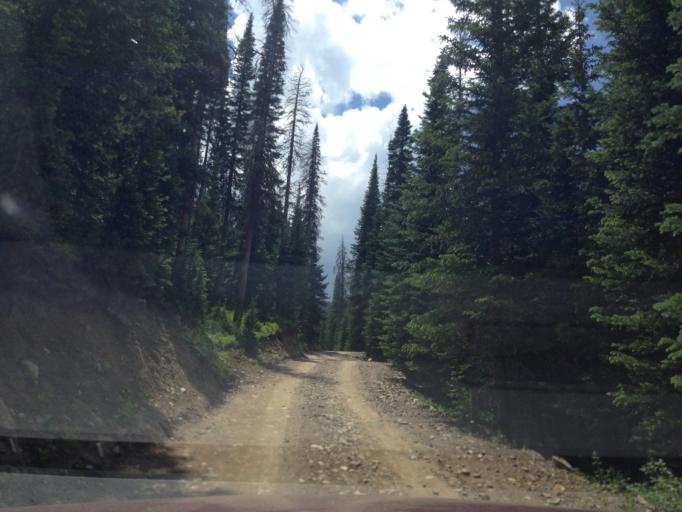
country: US
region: Colorado
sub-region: Larimer County
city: Estes Park
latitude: 40.4986
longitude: -105.8978
